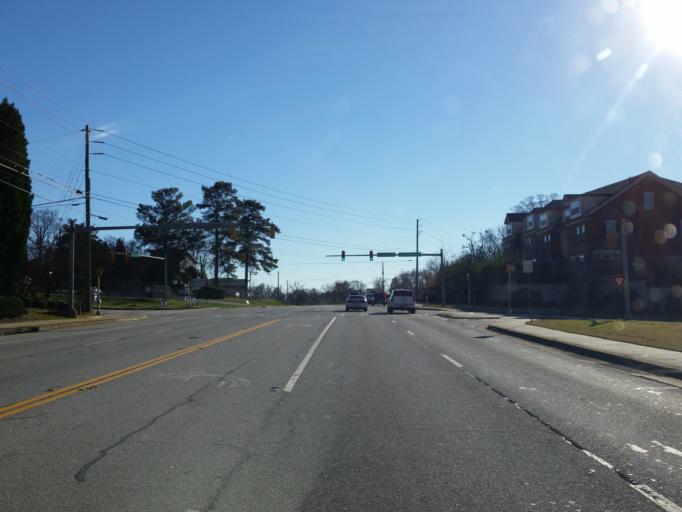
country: US
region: Georgia
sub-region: Cobb County
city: Vinings
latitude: 33.8551
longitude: -84.4926
